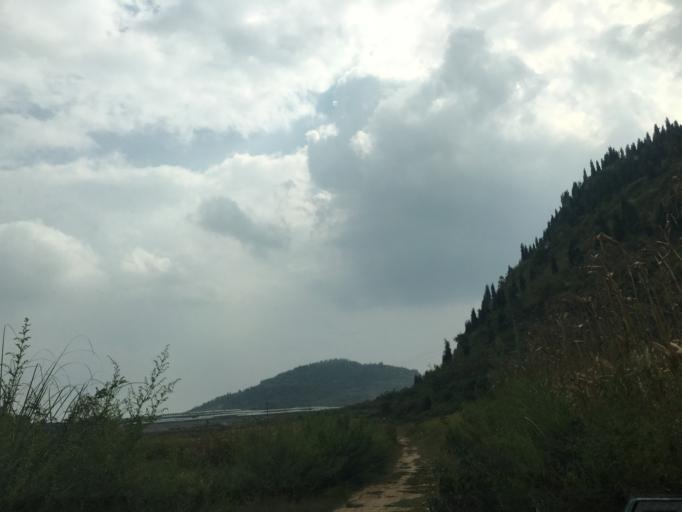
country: CN
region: Guangxi Zhuangzu Zizhiqu
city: Xinzhou
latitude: 25.4898
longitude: 105.6517
